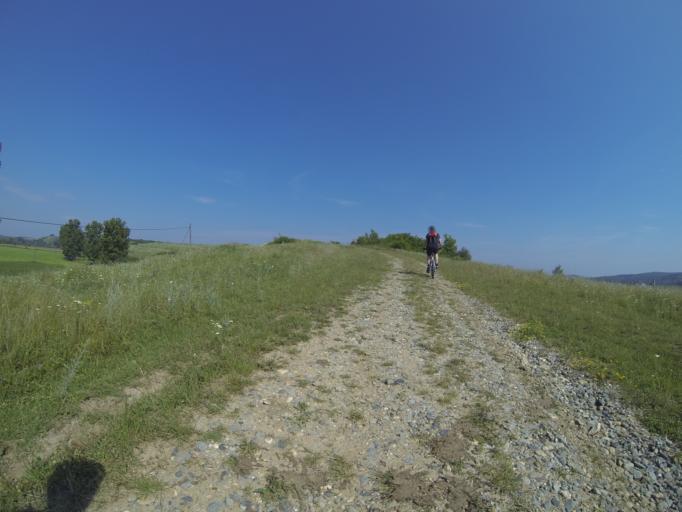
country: RO
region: Gorj
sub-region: Comuna Crusetu
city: Crusetu
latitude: 44.6057
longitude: 23.6804
